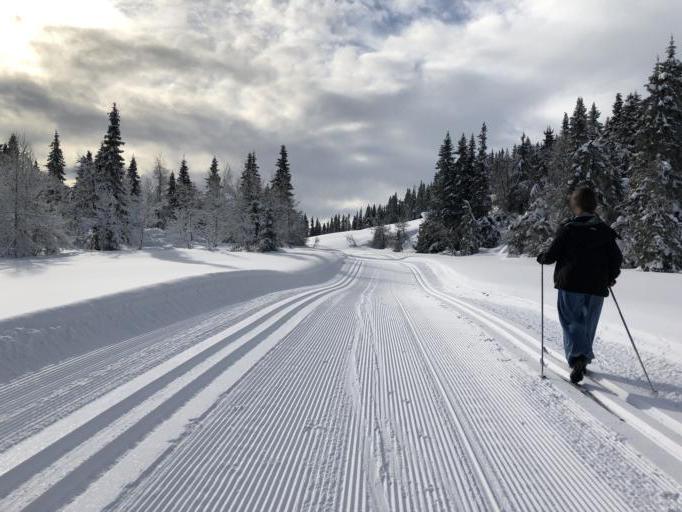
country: NO
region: Oppland
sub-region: Gausdal
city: Segalstad bru
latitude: 61.3199
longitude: 10.0579
